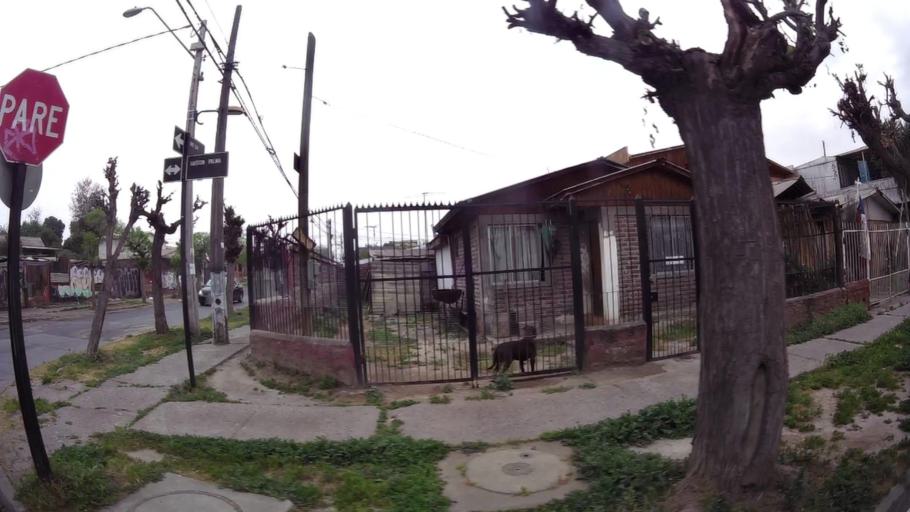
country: CL
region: Santiago Metropolitan
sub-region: Provincia de Santiago
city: Lo Prado
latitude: -33.5073
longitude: -70.7420
